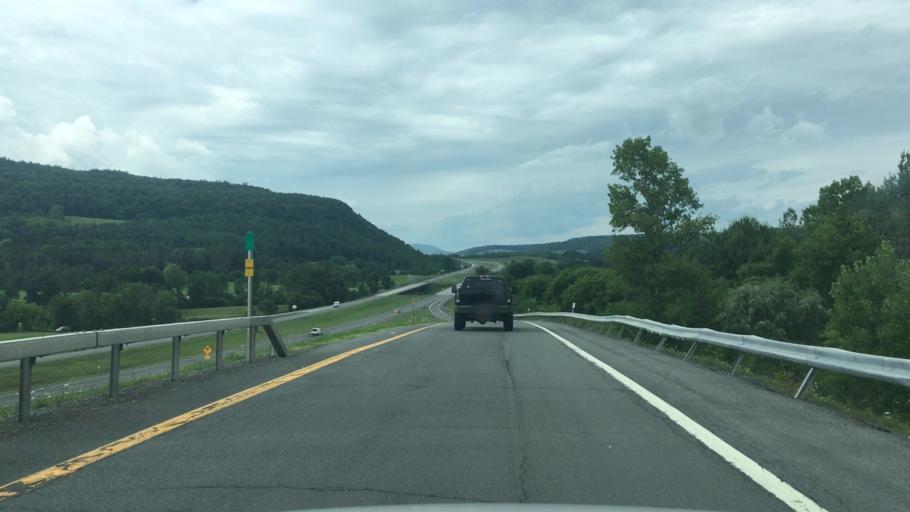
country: US
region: New York
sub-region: Schoharie County
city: Schoharie
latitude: 42.7078
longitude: -74.3145
